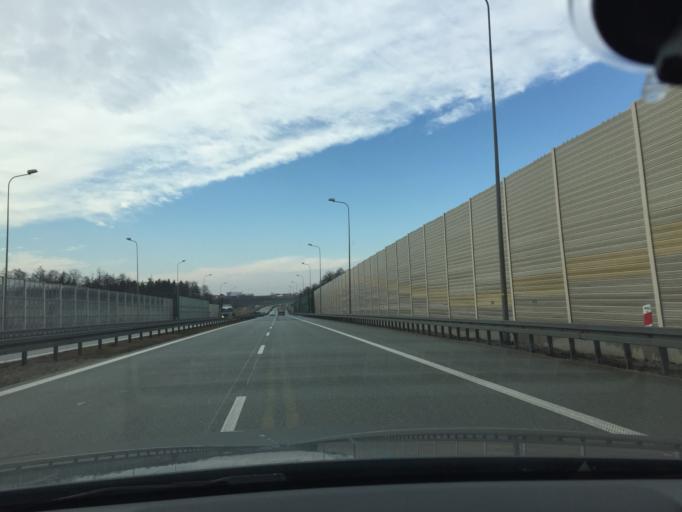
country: PL
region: Lodz Voivodeship
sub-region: Powiat skierniewicki
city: Kowiesy
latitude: 51.8905
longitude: 20.4205
